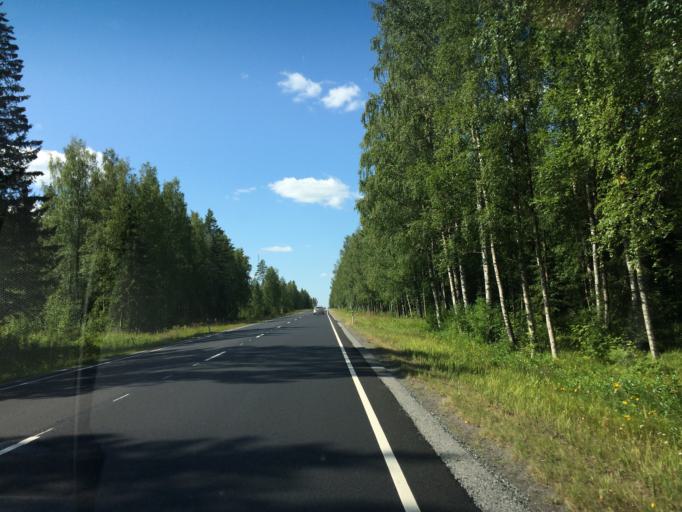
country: FI
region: Pirkanmaa
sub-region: Lounais-Pirkanmaa
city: Kiikoinen
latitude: 61.4743
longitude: 22.4867
